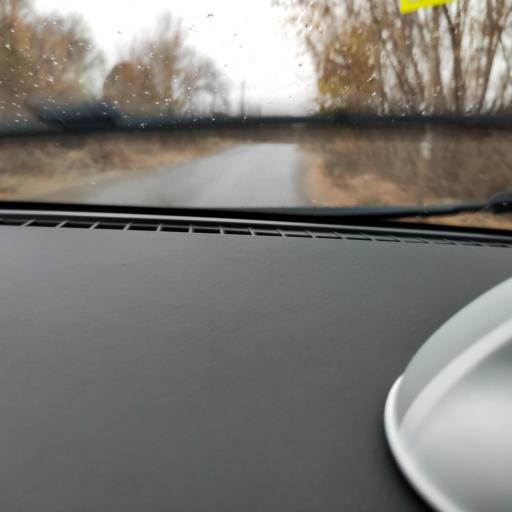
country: RU
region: Samara
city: Petra-Dubrava
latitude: 53.2962
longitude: 50.3047
